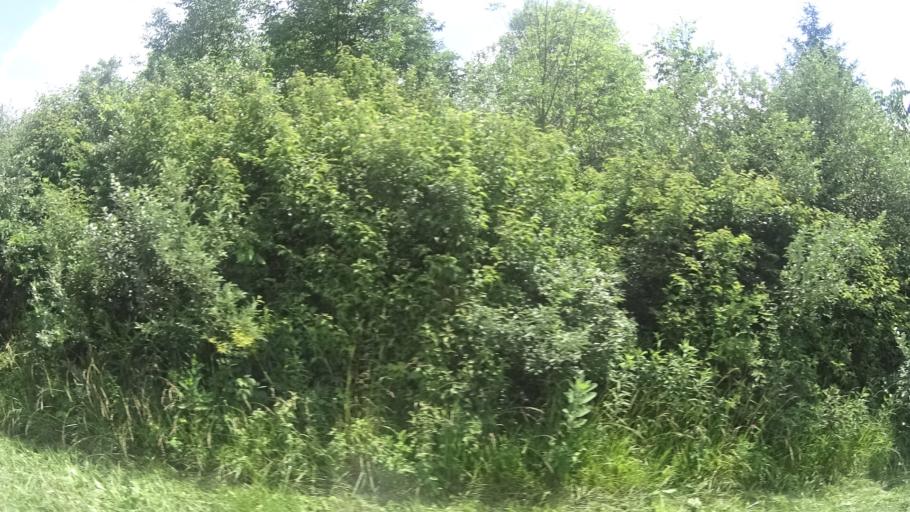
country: US
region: Ohio
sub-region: Lorain County
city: Camden
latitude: 41.2851
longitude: -82.3424
